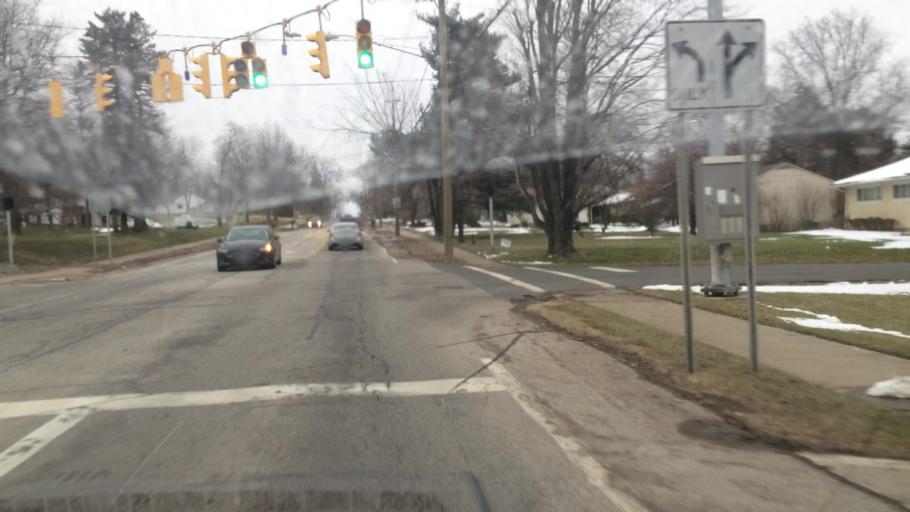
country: US
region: Ohio
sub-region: Cuyahoga County
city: Independence
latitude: 41.3448
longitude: -81.6592
